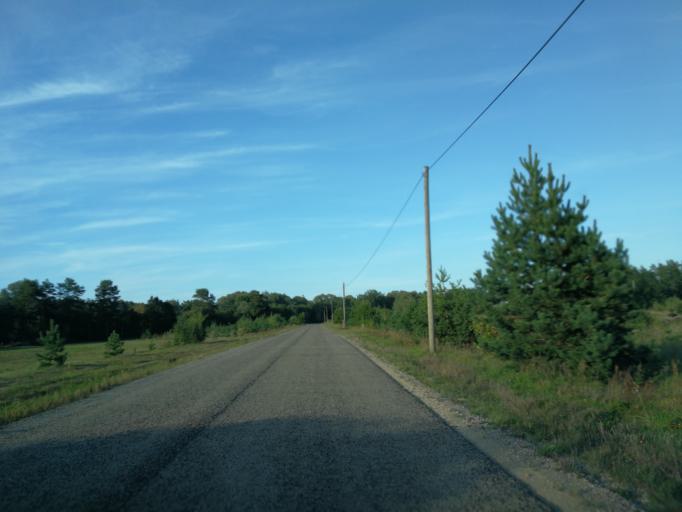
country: LV
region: Garkalne
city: Garkalne
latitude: 57.0792
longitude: 24.4613
